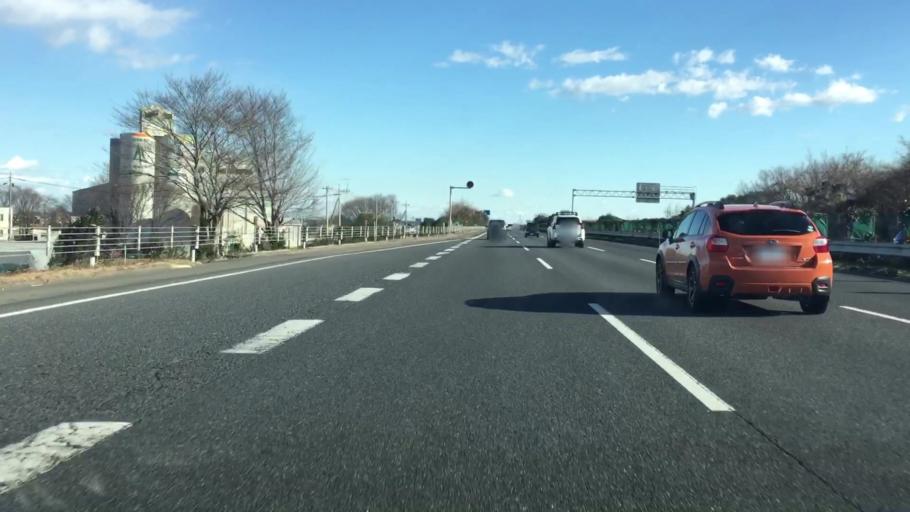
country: JP
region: Gunma
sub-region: Sawa-gun
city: Tamamura
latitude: 36.2538
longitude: 139.1242
